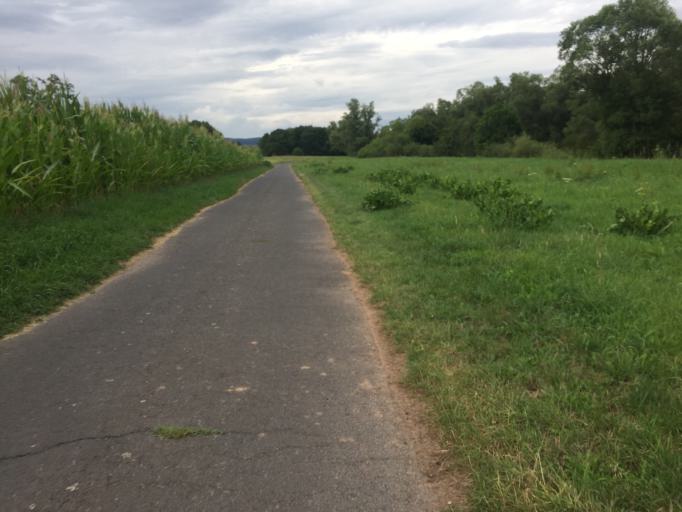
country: DE
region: Hesse
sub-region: Regierungsbezirk Kassel
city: Alheim
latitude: 51.0093
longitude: 9.6896
